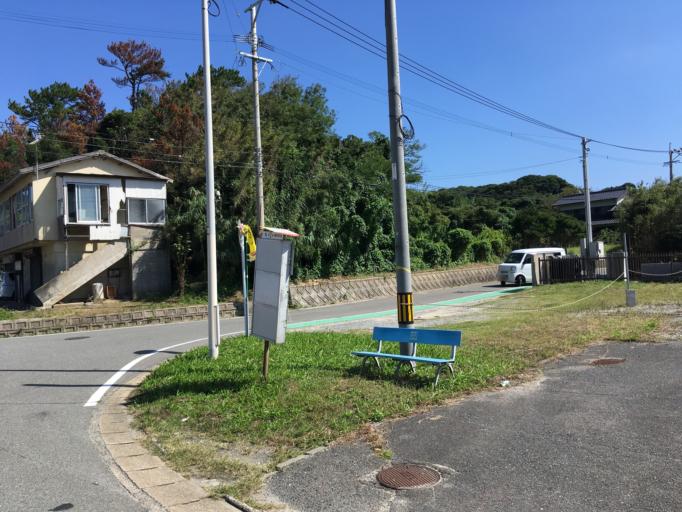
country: JP
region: Fukuoka
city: Shingu
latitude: 33.6868
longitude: 130.2943
